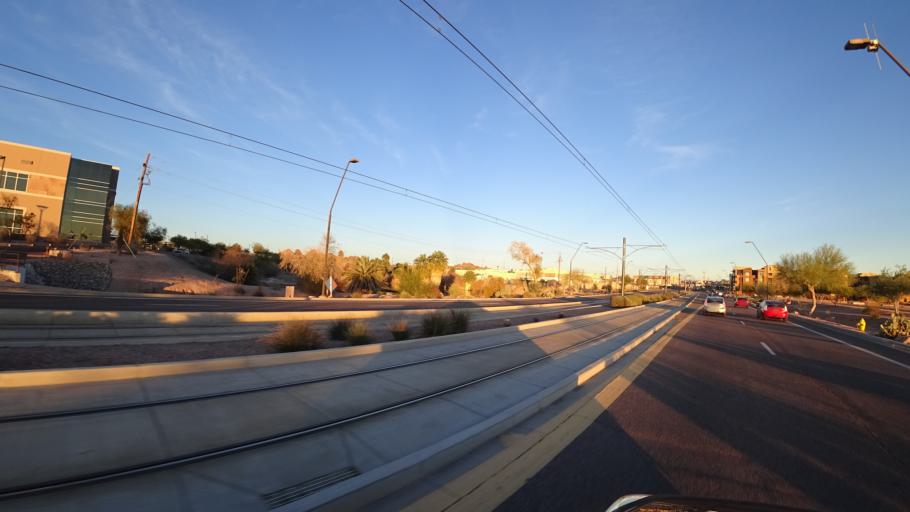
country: US
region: Arizona
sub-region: Maricopa County
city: Tempe Junction
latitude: 33.4402
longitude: -111.9531
